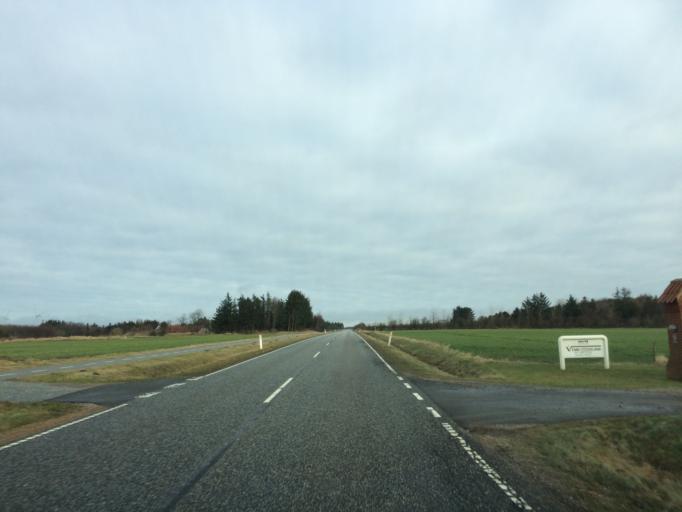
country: DK
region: Central Jutland
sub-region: Holstebro Kommune
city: Ulfborg
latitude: 56.3500
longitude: 8.3676
